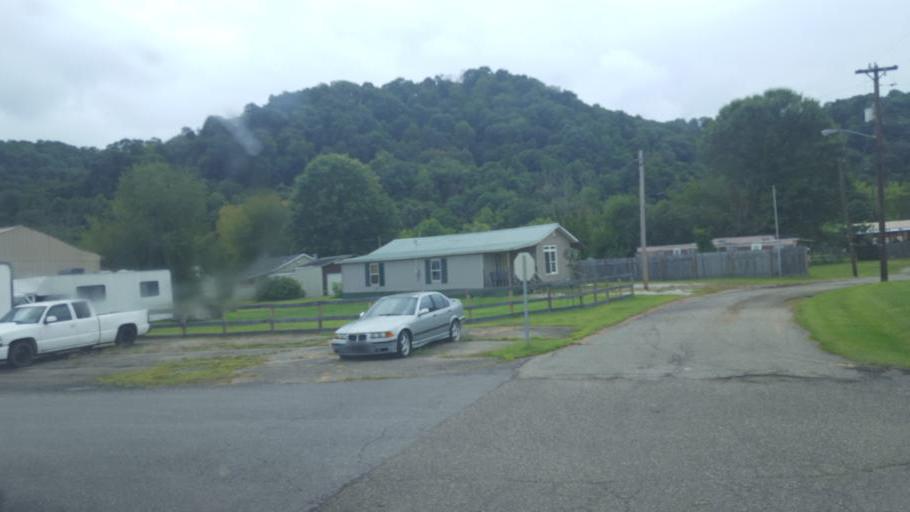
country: US
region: Kentucky
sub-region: Greenup County
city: South Shore
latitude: 38.7219
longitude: -82.9693
